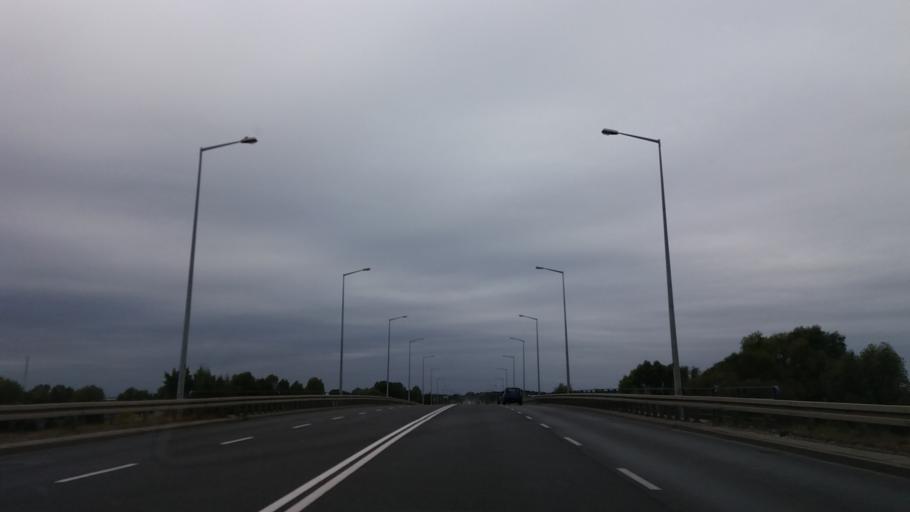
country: PL
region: Lubusz
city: Gorzow Wielkopolski
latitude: 52.7154
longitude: 15.2464
